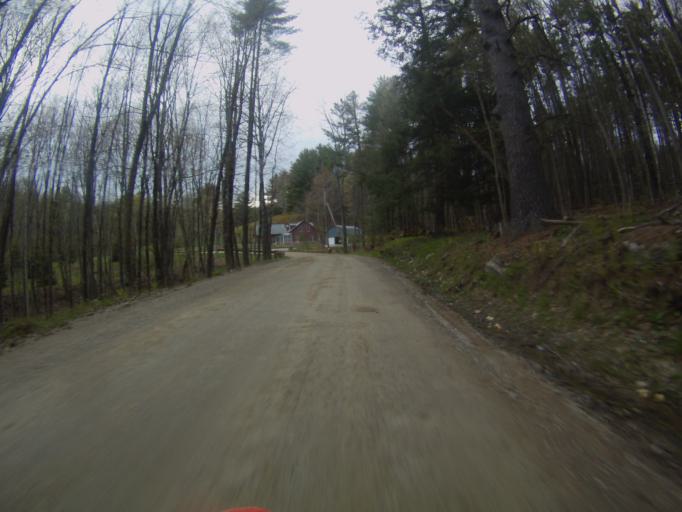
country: US
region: Vermont
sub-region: Addison County
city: Middlebury (village)
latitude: 43.9824
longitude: -73.0608
